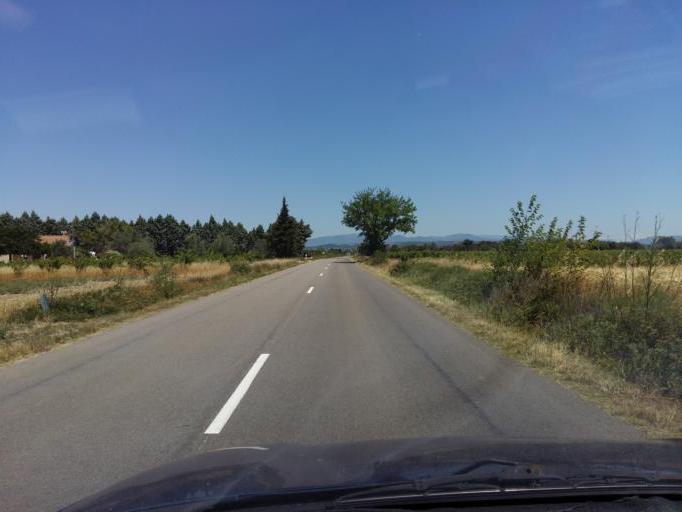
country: FR
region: Provence-Alpes-Cote d'Azur
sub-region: Departement du Vaucluse
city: Sainte-Cecile-les-Vignes
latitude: 44.2634
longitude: 4.9009
